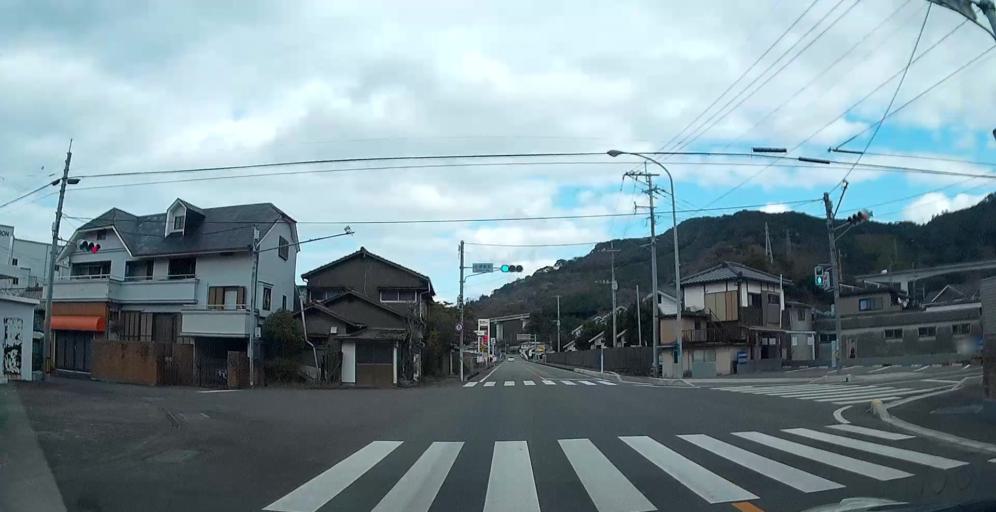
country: JP
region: Kumamoto
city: Minamata
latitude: 32.3507
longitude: 130.5058
